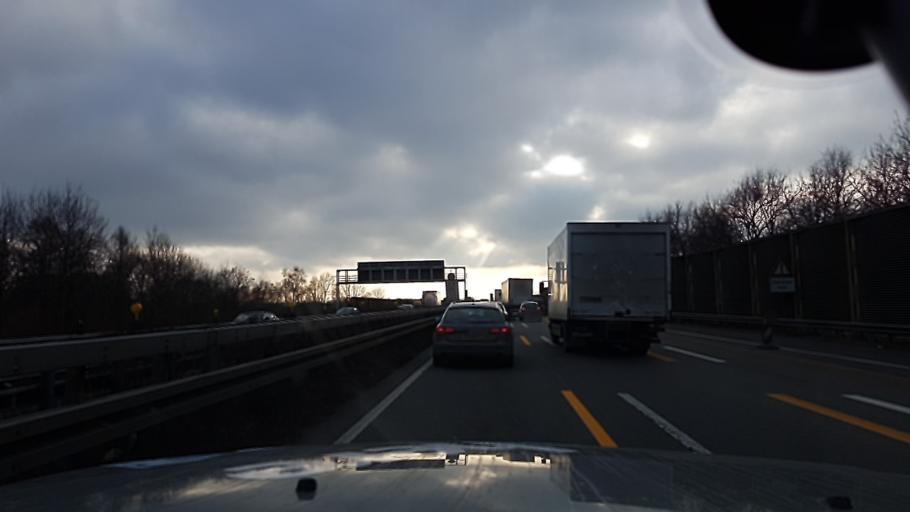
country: DE
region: North Rhine-Westphalia
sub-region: Regierungsbezirk Munster
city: Lotte
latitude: 52.2998
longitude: 7.9426
